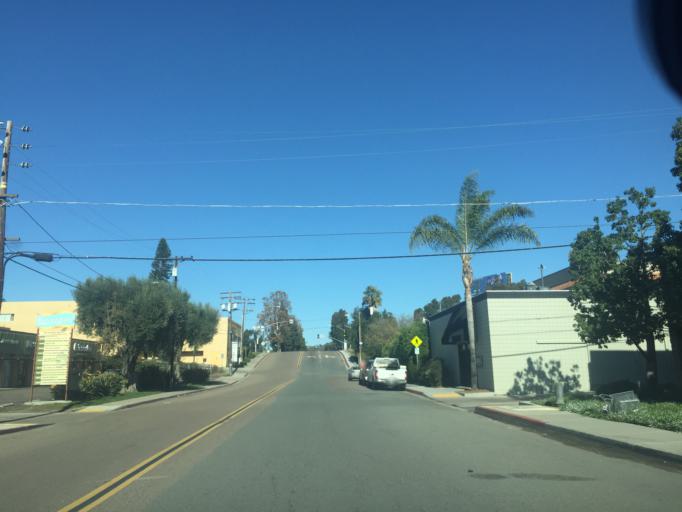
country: US
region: California
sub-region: San Diego County
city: La Mesa
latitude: 32.7890
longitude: -117.0996
